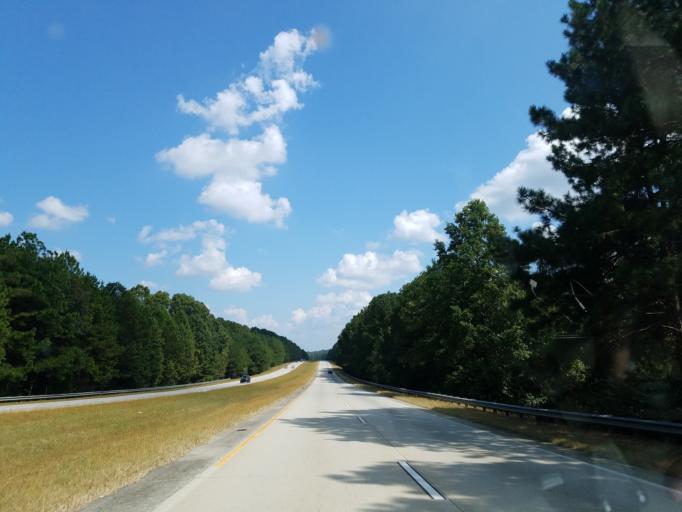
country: US
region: Georgia
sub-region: Barrow County
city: Russell
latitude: 33.9517
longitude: -83.6862
